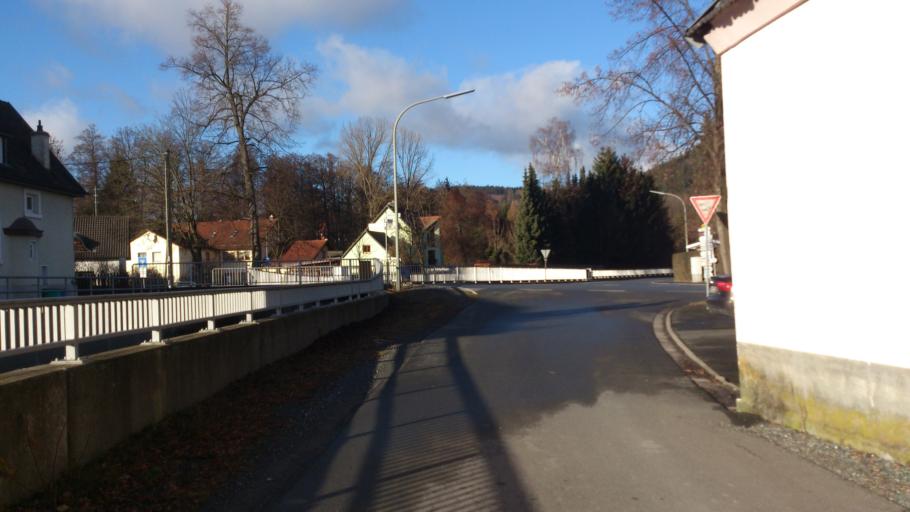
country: DE
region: Bavaria
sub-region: Upper Franconia
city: Stadtsteinach
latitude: 50.1640
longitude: 11.5066
